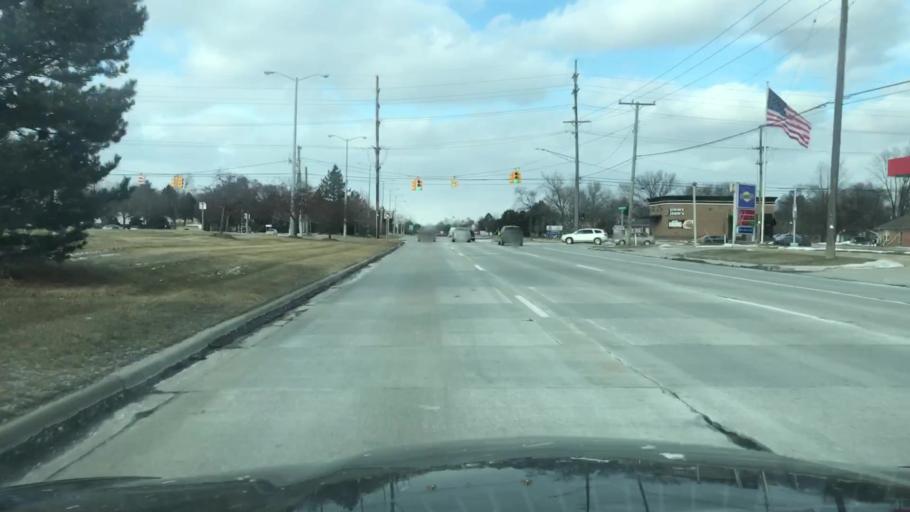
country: US
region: Michigan
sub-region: Macomb County
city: Utica
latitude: 42.6079
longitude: -83.0511
